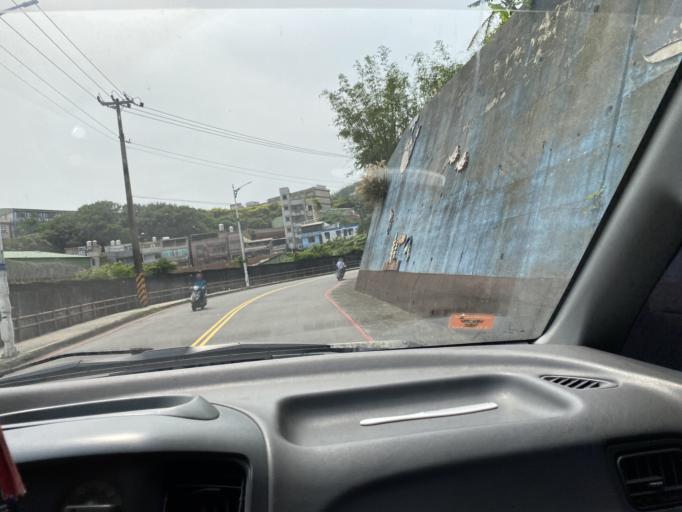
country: TW
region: Taiwan
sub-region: Keelung
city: Keelung
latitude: 25.1570
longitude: 121.7308
